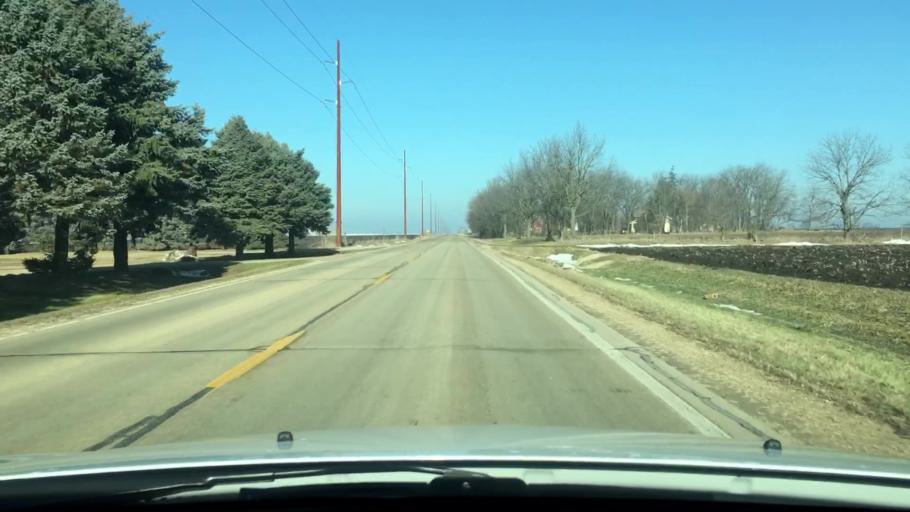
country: US
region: Illinois
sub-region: Ogle County
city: Rochelle
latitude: 41.8540
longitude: -89.0247
